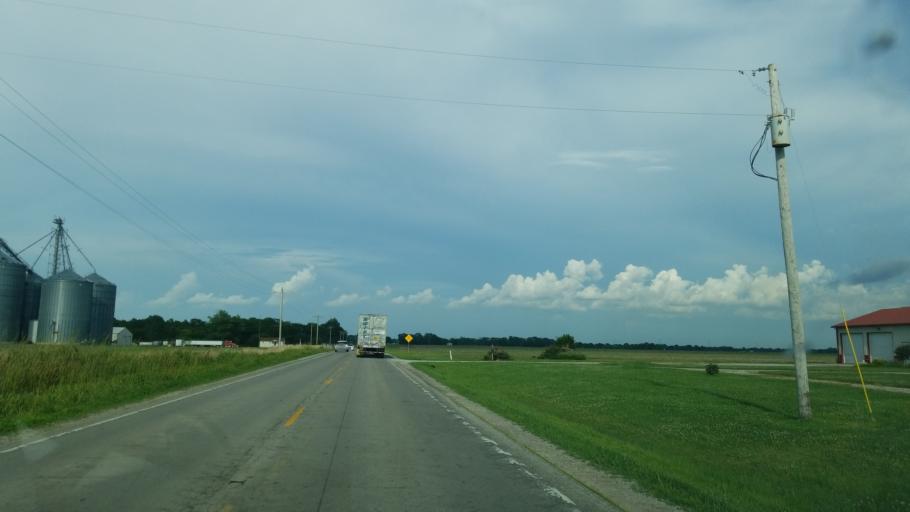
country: US
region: Illinois
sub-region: Marion County
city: Sandoval
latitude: 38.6165
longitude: -89.1545
